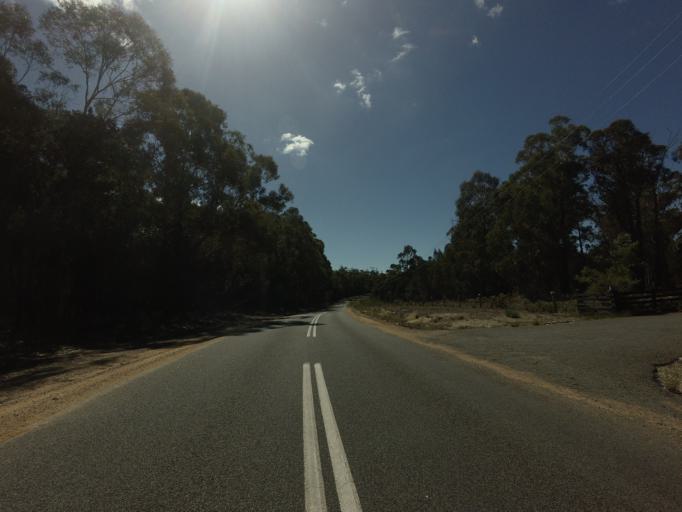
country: AU
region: Tasmania
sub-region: Break O'Day
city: St Helens
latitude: -41.6742
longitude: 148.2779
